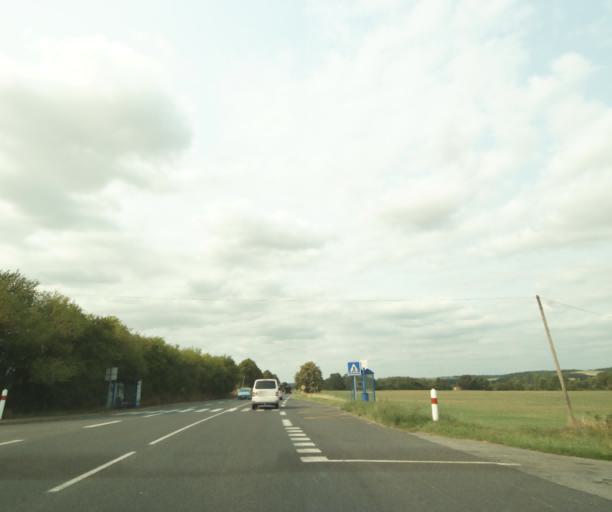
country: FR
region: Centre
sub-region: Departement de l'Indre
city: Chatillon-sur-Indre
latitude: 47.0328
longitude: 1.0957
